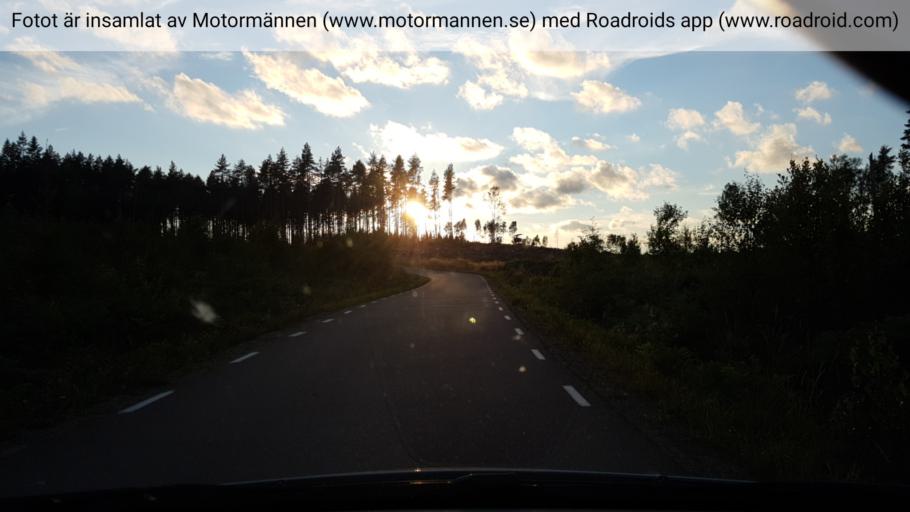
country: SE
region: Vaestmanland
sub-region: Surahammars Kommun
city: Ramnas
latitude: 59.7065
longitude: 16.1192
